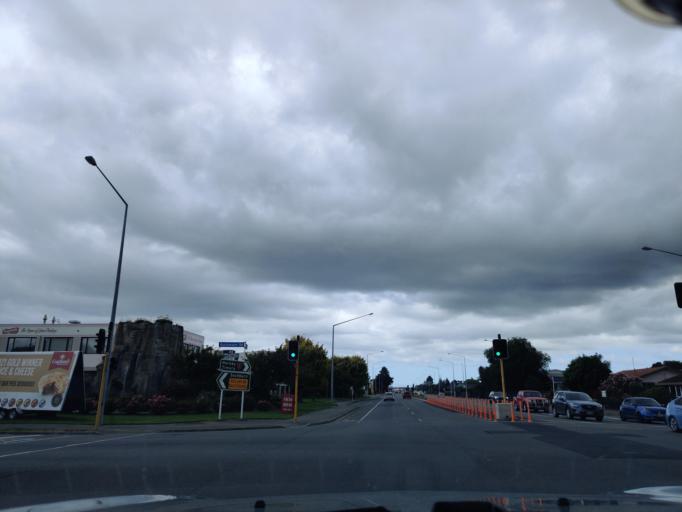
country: NZ
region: Canterbury
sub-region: Selwyn District
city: Prebbleton
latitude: -43.5314
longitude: 172.5321
